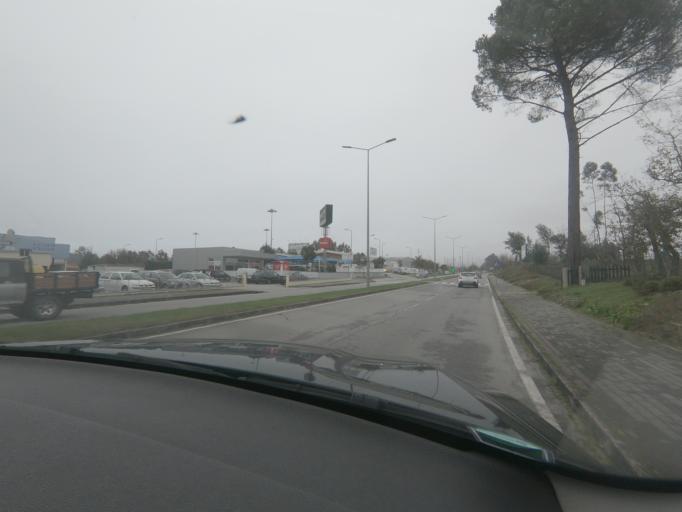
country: PT
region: Viseu
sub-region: Concelho de Tondela
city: Tondela
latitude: 40.5278
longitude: -8.0887
